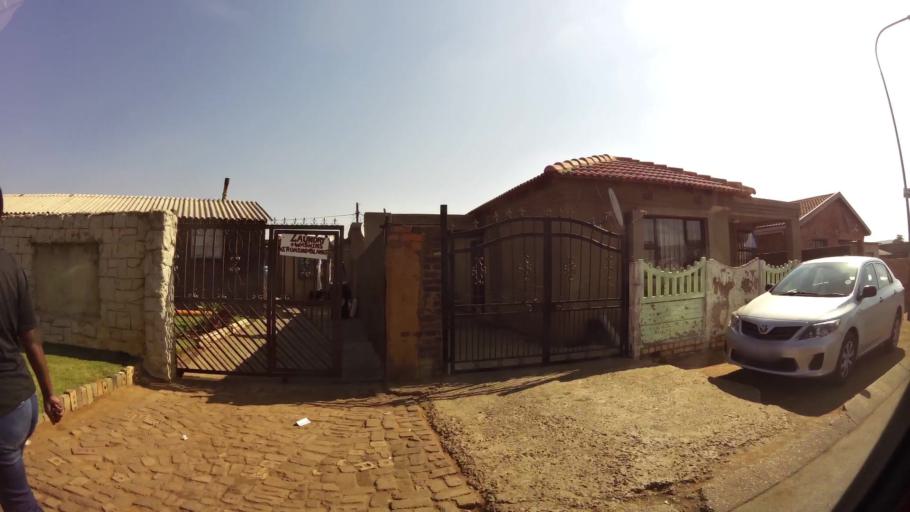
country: ZA
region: Gauteng
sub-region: City of Johannesburg Metropolitan Municipality
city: Johannesburg
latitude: -26.2448
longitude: 27.9586
